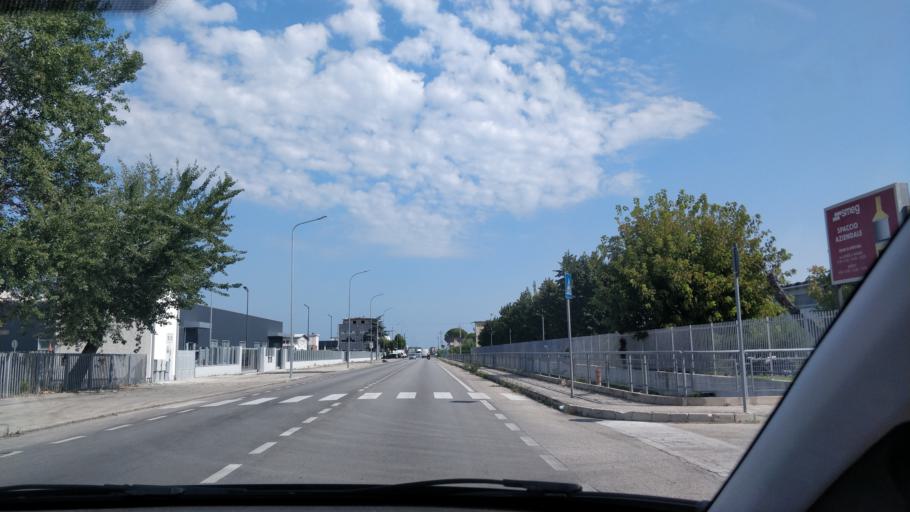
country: IT
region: Abruzzo
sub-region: Provincia di Pescara
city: Santa Teresa
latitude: 42.4086
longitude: 14.1652
